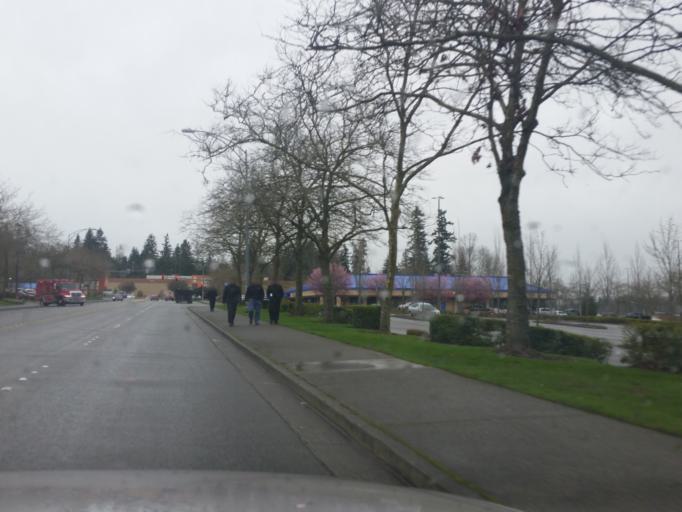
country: US
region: Washington
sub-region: Snohomish County
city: Alderwood Manor
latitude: 47.8301
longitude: -122.2777
